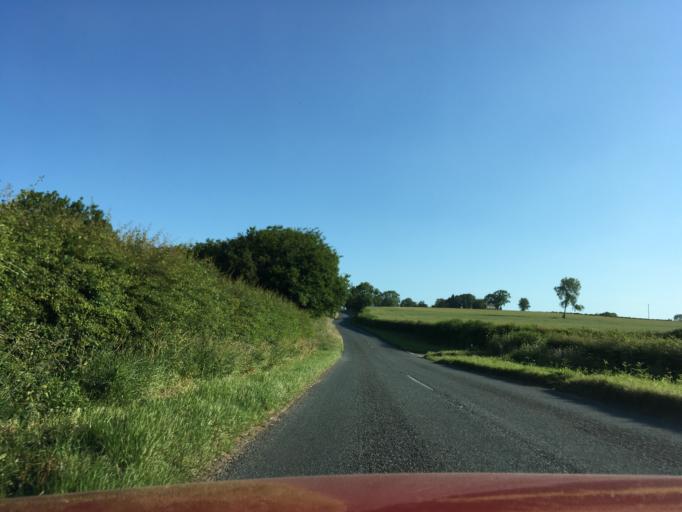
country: GB
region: Wales
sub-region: Monmouthshire
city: Tintern
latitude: 51.7113
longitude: -2.6316
